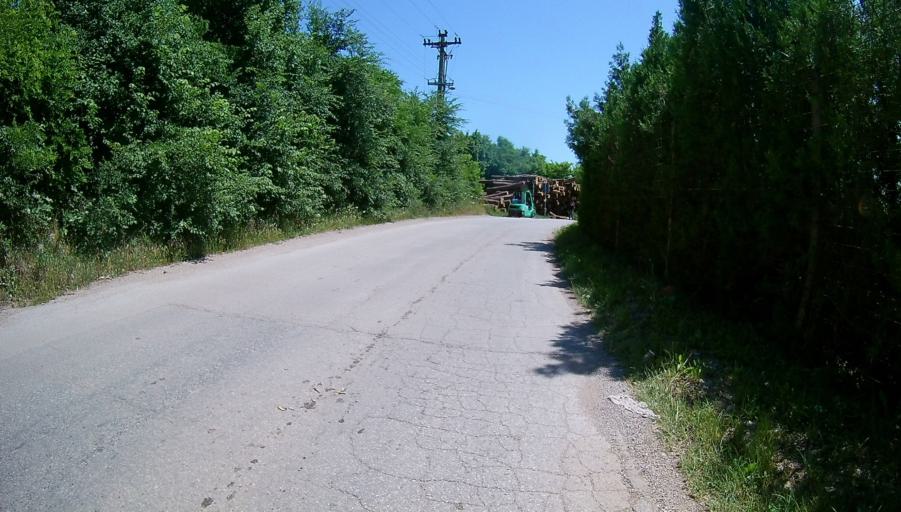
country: RS
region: Central Serbia
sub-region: Nisavski Okrug
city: Nis
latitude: 43.2906
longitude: 21.9014
